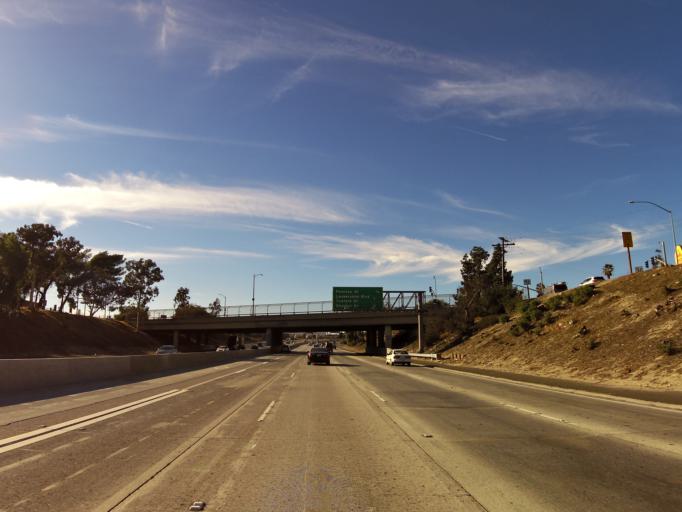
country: US
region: California
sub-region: Los Angeles County
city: North Hollywood
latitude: 34.2220
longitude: -118.3654
